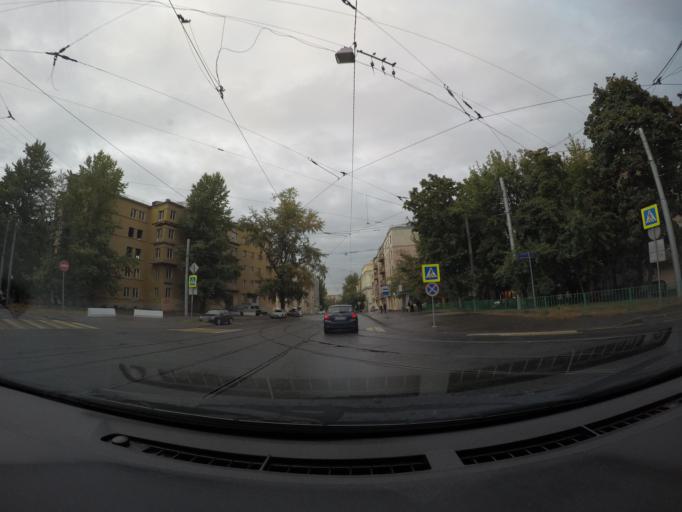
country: RU
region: Moscow
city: Lefortovo
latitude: 55.7903
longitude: 37.6951
